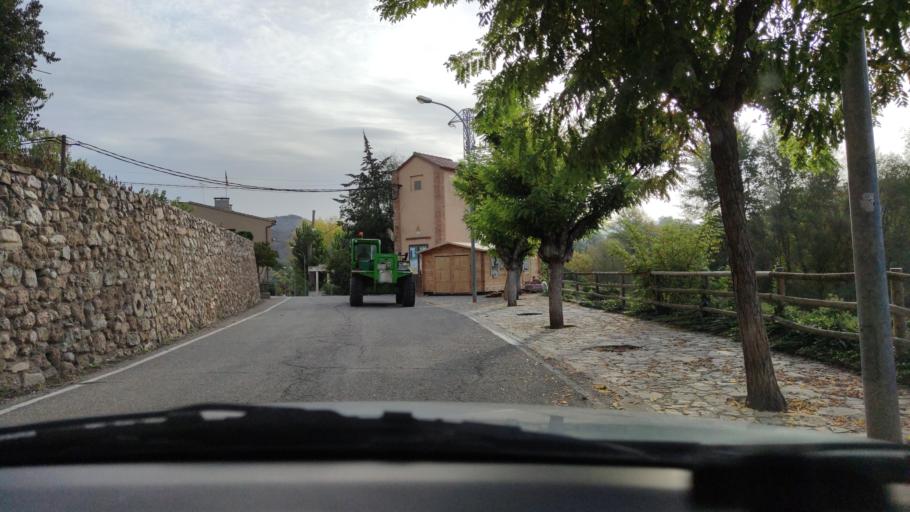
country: ES
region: Catalonia
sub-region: Provincia de Lleida
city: Cubells
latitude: 41.9117
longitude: 0.9610
